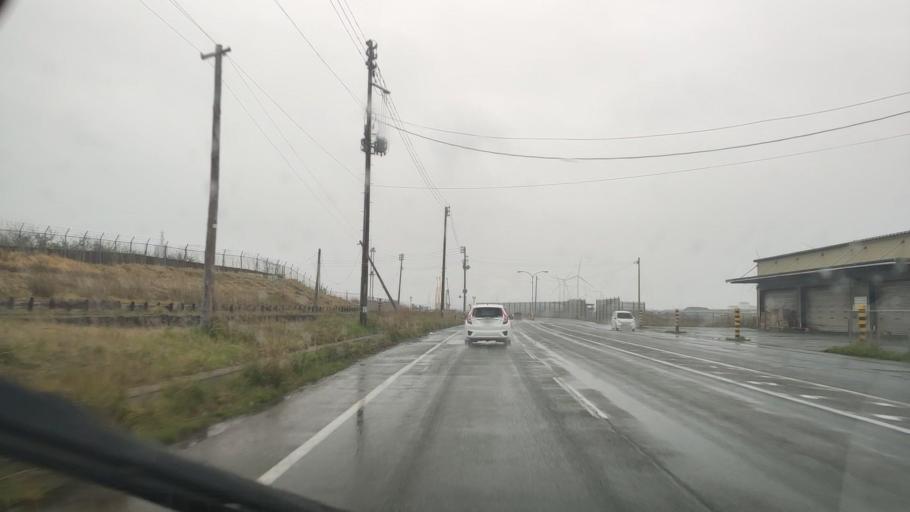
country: JP
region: Akita
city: Akita Shi
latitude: 39.7627
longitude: 140.0511
